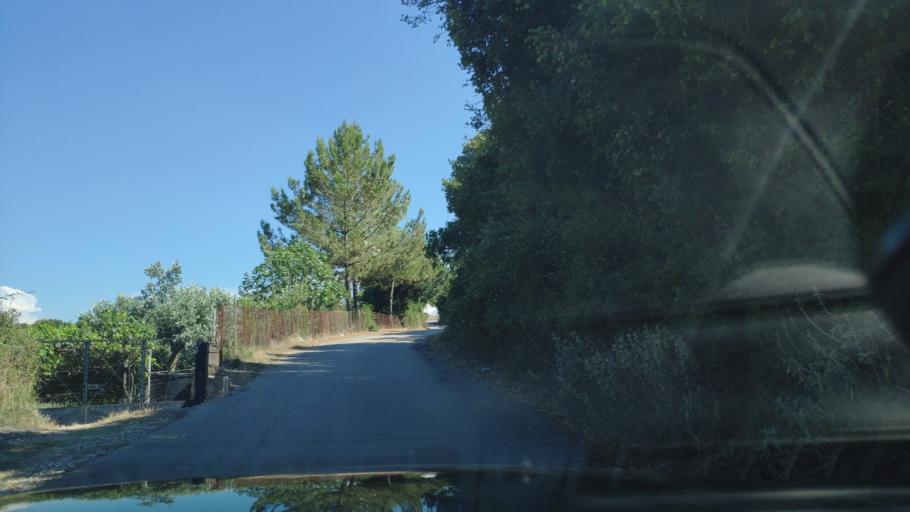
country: GR
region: West Greece
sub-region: Nomos Aitolias kai Akarnanias
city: Katouna
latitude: 38.7949
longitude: 21.1146
